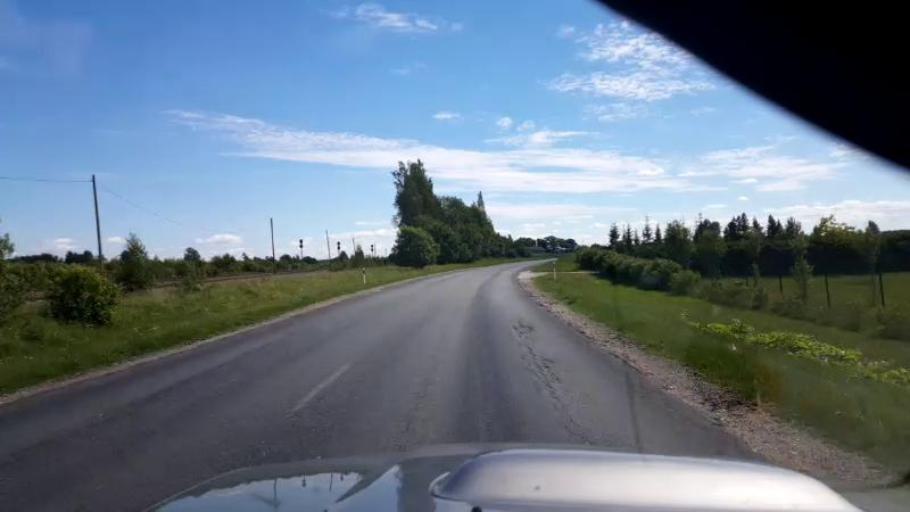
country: EE
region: Laeaene-Virumaa
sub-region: Rakke vald
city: Rakke
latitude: 58.9059
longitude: 26.2808
